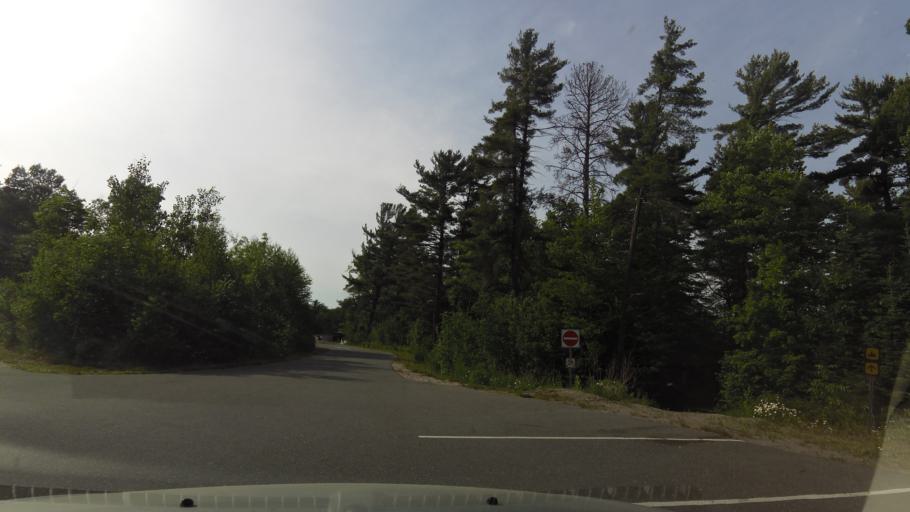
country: CA
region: Ontario
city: Greater Sudbury
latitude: 46.0160
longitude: -80.5844
